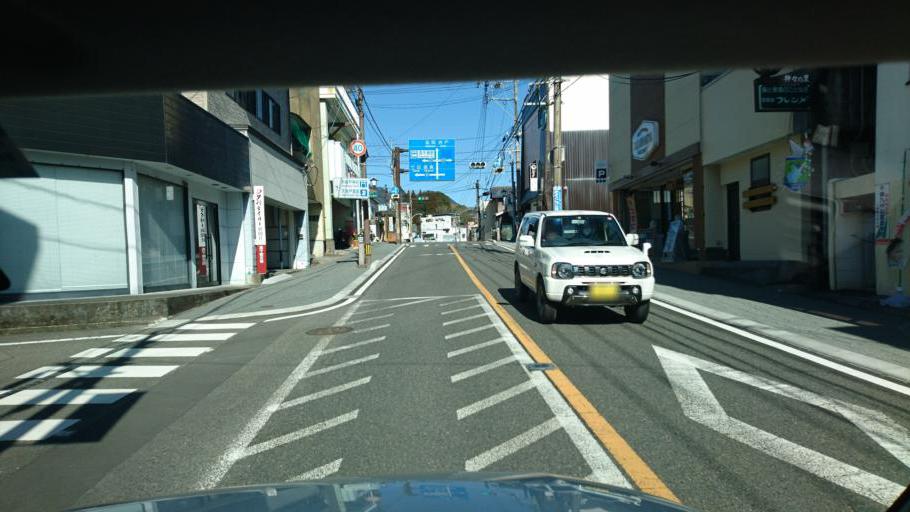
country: JP
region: Oita
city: Takedamachi
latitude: 32.7098
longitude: 131.3073
